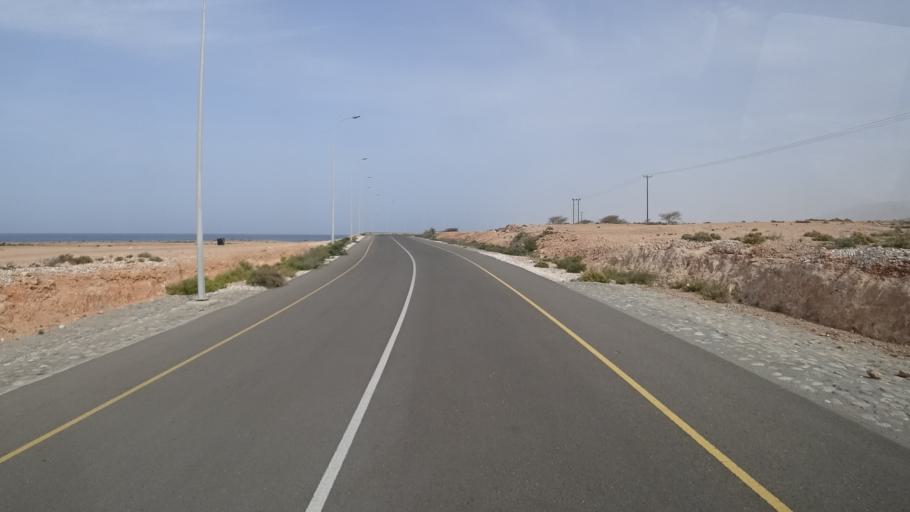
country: OM
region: Ash Sharqiyah
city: Sur
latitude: 23.0052
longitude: 59.1143
